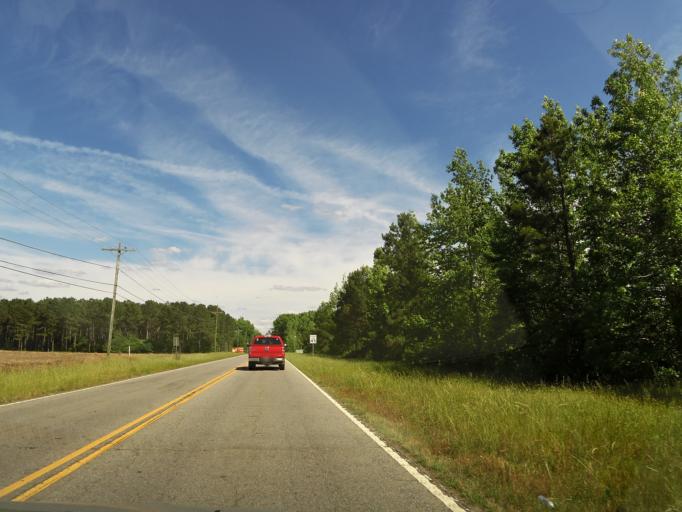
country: US
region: South Carolina
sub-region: Bamberg County
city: Denmark
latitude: 33.3324
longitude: -81.1569
